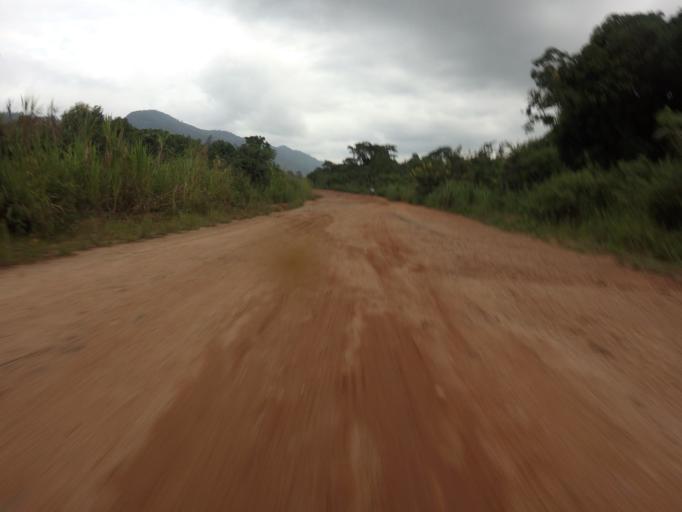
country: GH
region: Volta
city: Ho
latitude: 6.7776
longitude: 0.3647
